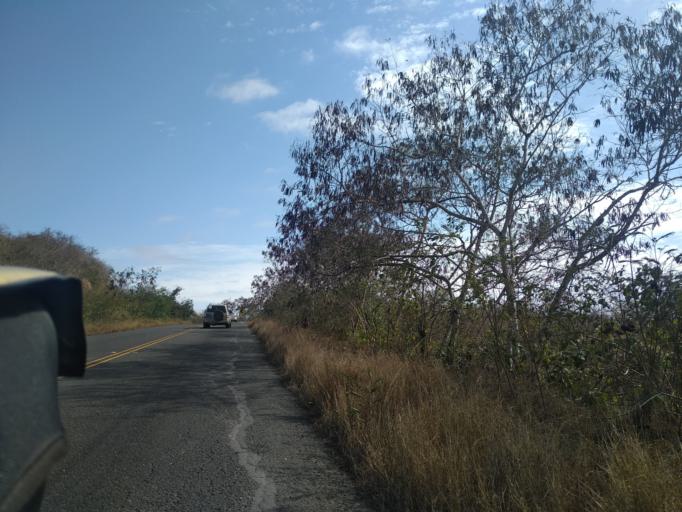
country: EC
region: Manabi
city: Jipijapa
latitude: -1.4597
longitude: -80.7625
